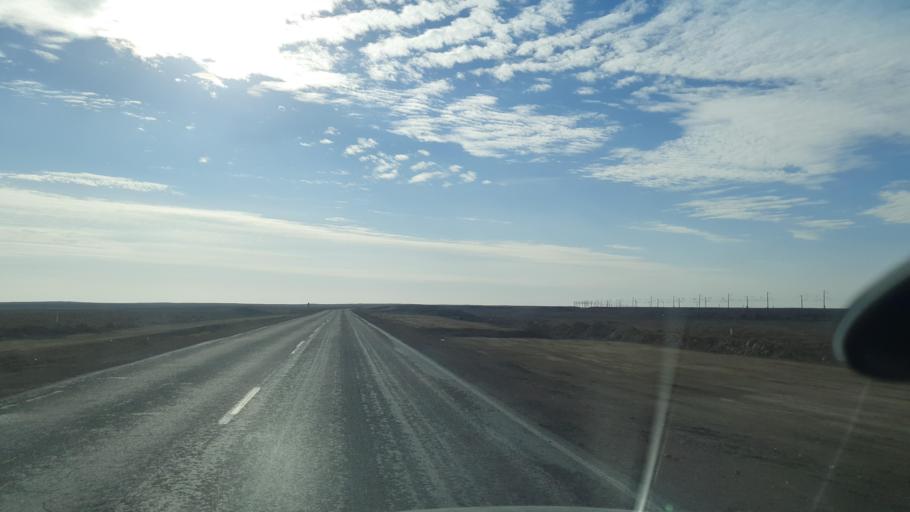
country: KZ
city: Priozersk
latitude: 45.9043
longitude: 73.5123
